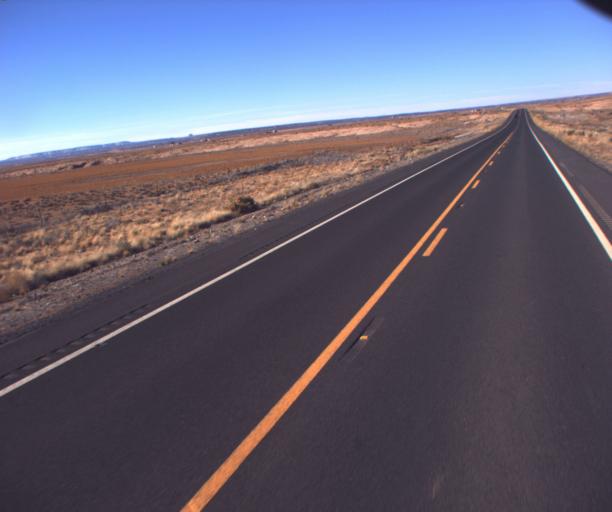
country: US
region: Arizona
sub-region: Coconino County
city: Kaibito
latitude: 36.4735
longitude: -110.6990
